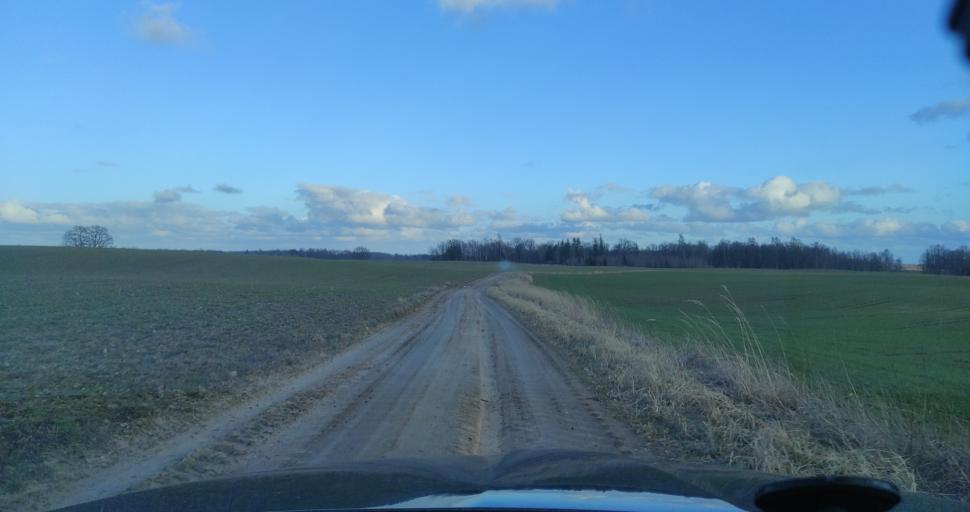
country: LV
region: Aizpute
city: Aizpute
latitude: 56.8704
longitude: 21.7558
